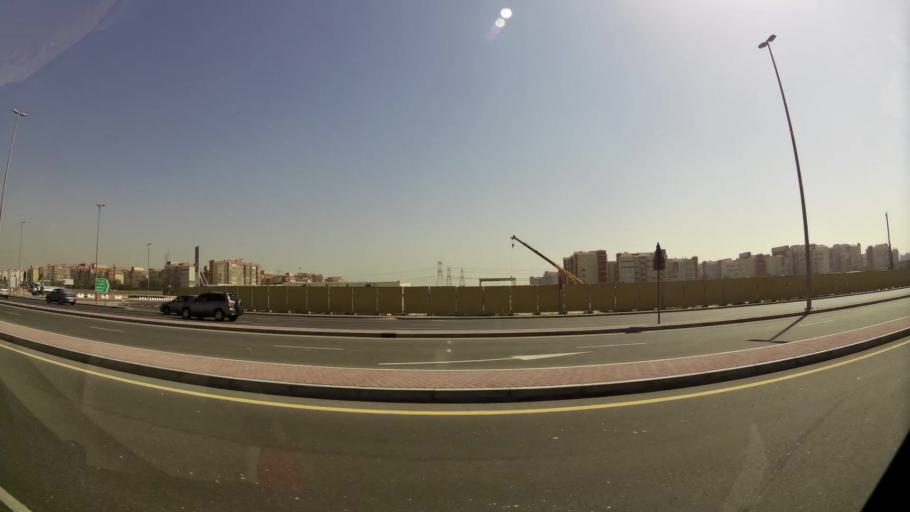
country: AE
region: Dubai
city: Dubai
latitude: 25.0356
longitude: 55.1436
